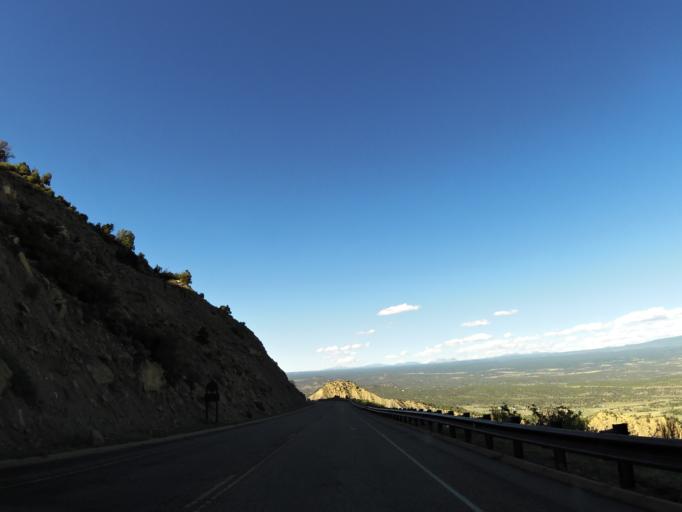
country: US
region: Colorado
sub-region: Montezuma County
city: Mancos
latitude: 37.3123
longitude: -108.4156
